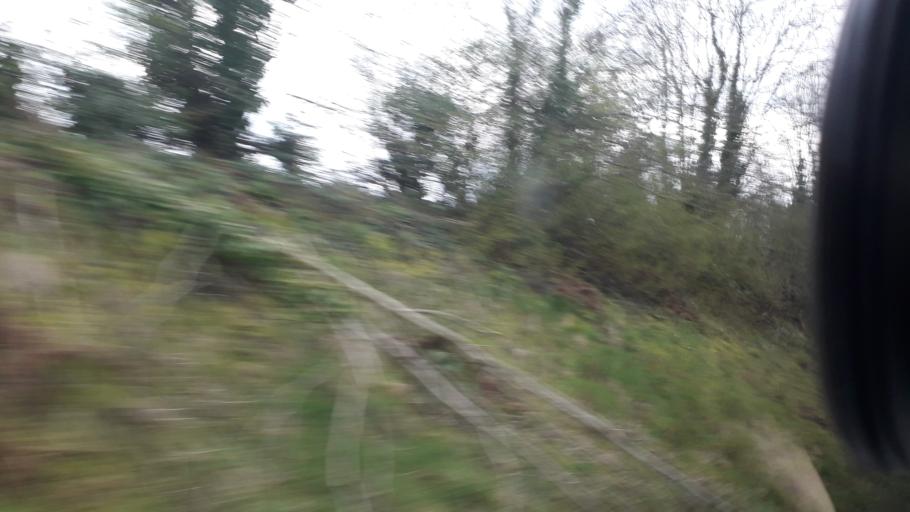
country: IE
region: Leinster
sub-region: An Longfort
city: Longford
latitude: 53.7059
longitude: -7.7134
